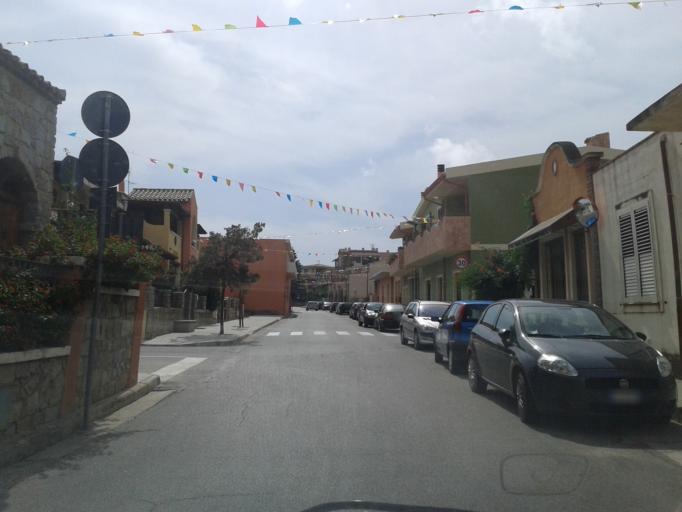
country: IT
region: Sardinia
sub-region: Provincia di Cagliari
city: Villasimius
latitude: 39.1451
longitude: 9.5196
